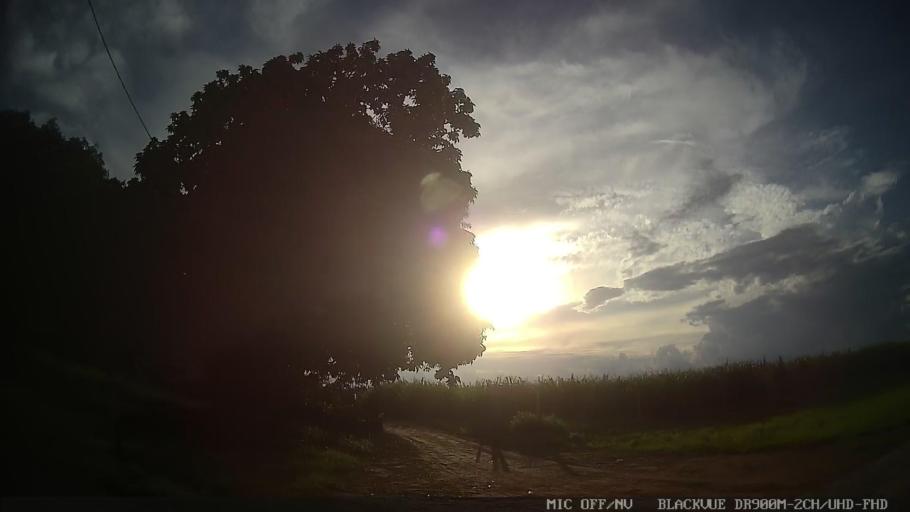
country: BR
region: Sao Paulo
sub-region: Cerquilho
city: Cerquilho
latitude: -23.1749
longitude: -47.6415
